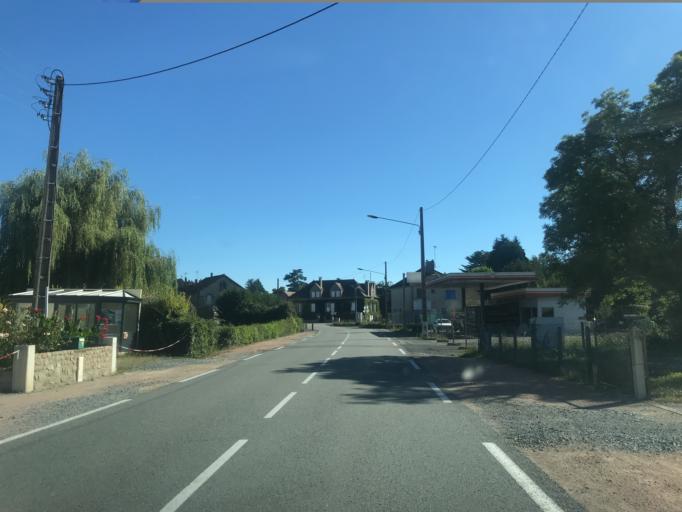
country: FR
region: Limousin
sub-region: Departement de la Creuse
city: Gouzon
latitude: 46.1887
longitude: 2.2372
